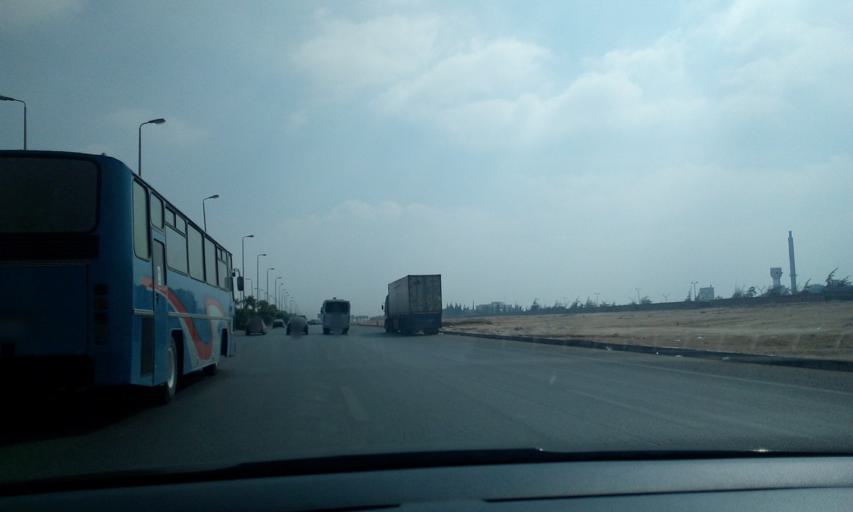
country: EG
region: Eastern Province
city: Bilbays
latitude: 30.2519
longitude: 31.7364
